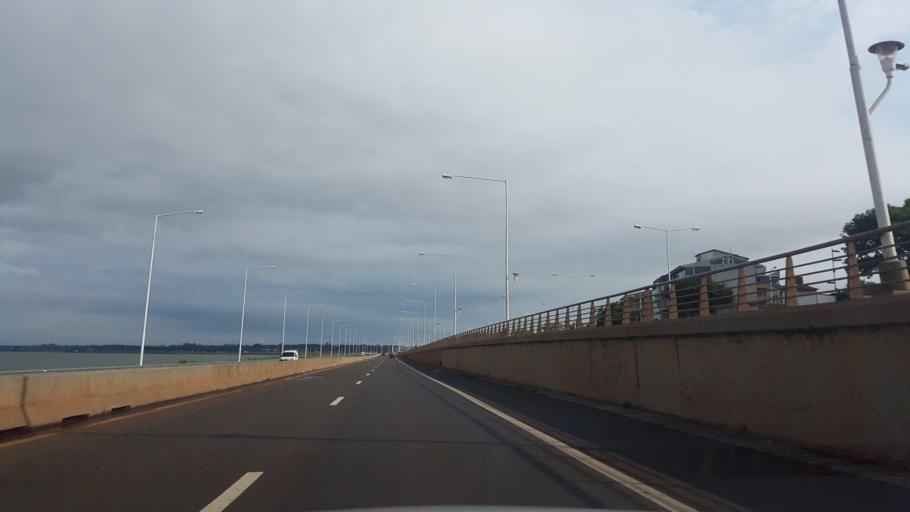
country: AR
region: Misiones
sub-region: Departamento de Capital
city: Posadas
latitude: -27.3969
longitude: -55.8927
